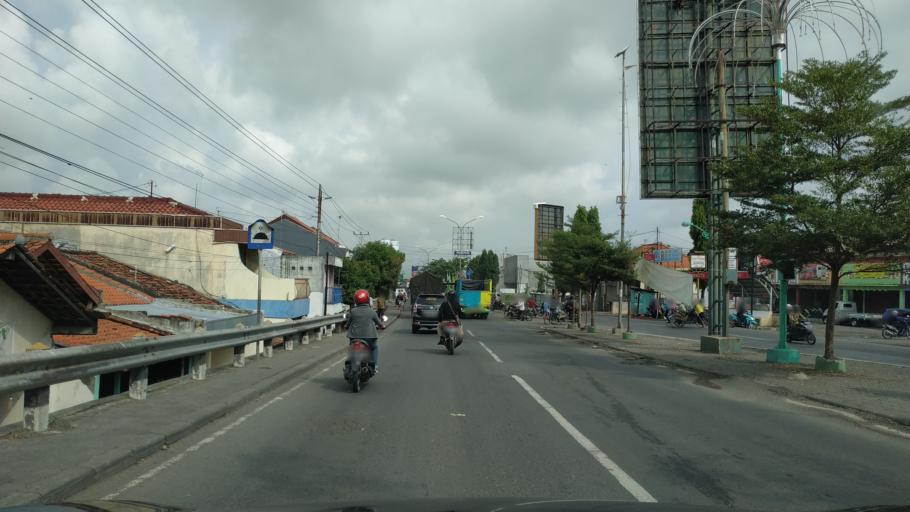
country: ID
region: Central Java
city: Dukuhturi
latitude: -6.8692
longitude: 109.0337
